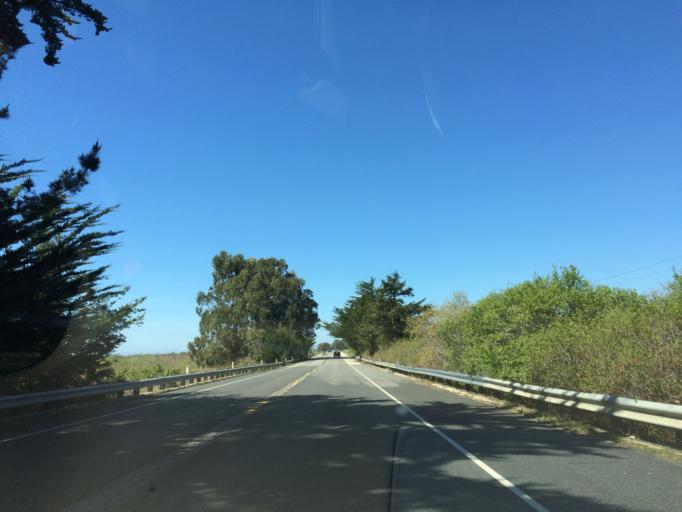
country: US
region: California
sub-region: Santa Cruz County
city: Bonny Doon
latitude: 37.1431
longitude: -122.3288
